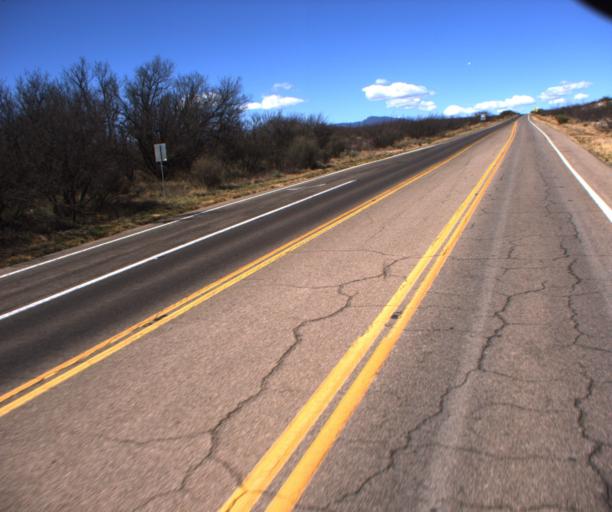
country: US
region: Arizona
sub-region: Cochise County
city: Sierra Vista Southeast
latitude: 31.5503
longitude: -110.1435
